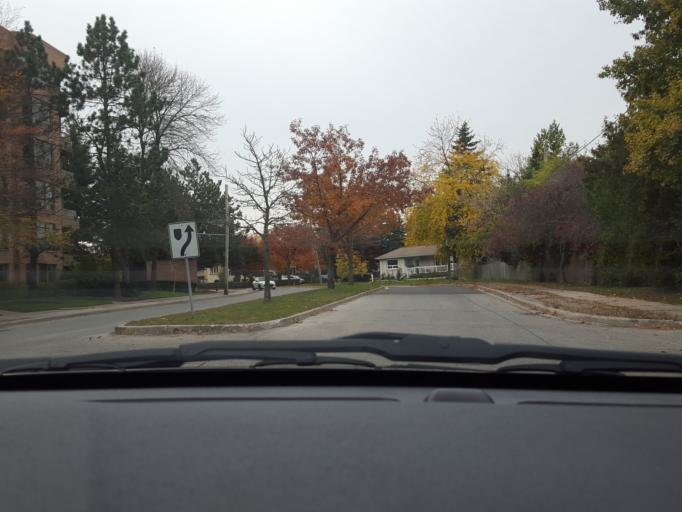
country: CA
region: Ontario
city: Willowdale
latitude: 43.7408
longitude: -79.3451
